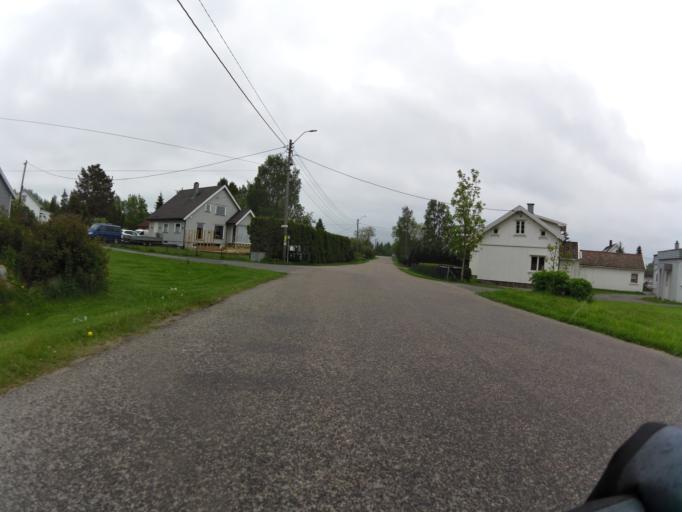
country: NO
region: Ostfold
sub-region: Rygge
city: Ryggebyen
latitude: 59.3659
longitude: 10.7756
